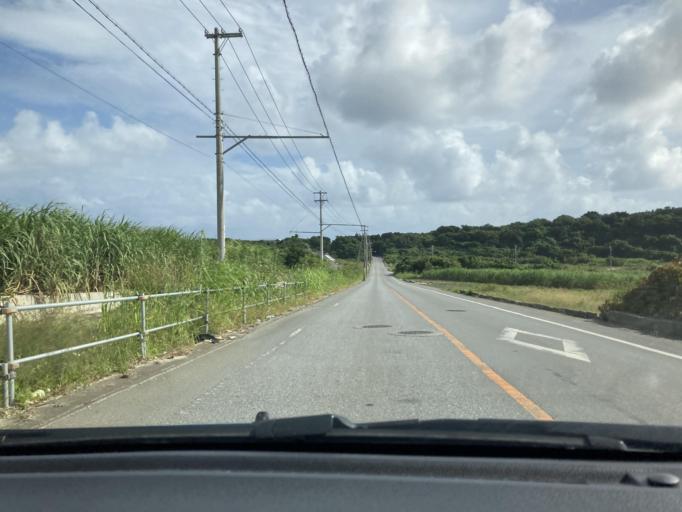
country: JP
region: Okinawa
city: Itoman
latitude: 26.1018
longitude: 127.6970
